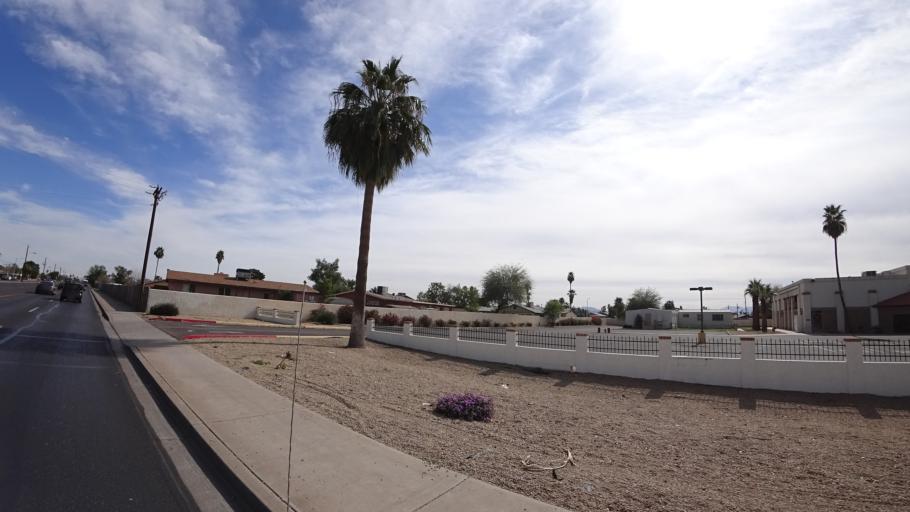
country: US
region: Arizona
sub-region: Maricopa County
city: Glendale
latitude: 33.4805
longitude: -112.1829
